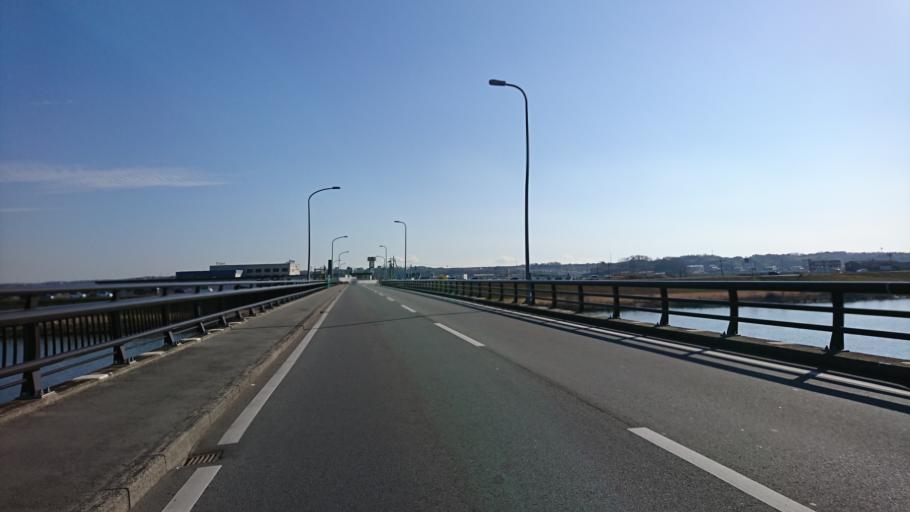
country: JP
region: Hyogo
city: Ono
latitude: 34.7974
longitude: 134.8998
